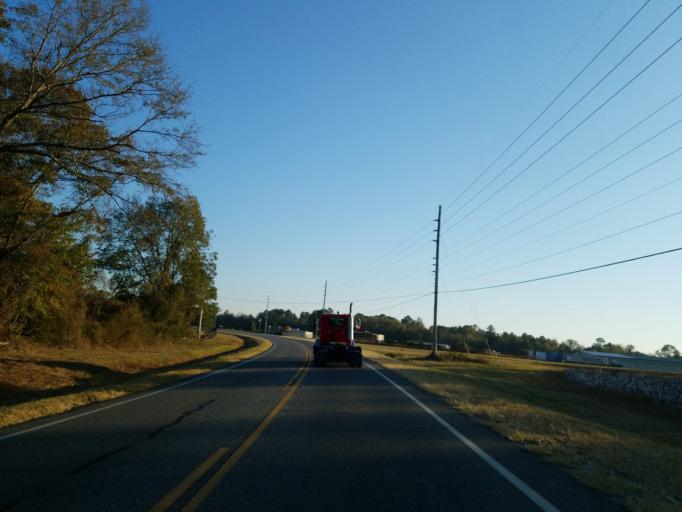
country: US
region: Georgia
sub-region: Crisp County
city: Cordele
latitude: 31.9516
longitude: -83.7461
